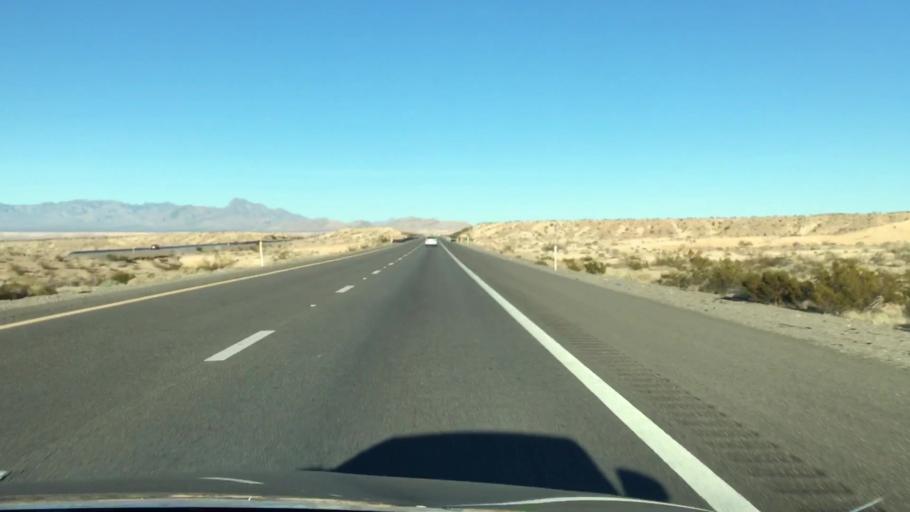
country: US
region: Nevada
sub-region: Clark County
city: Moapa Town
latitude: 36.6066
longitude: -114.6331
